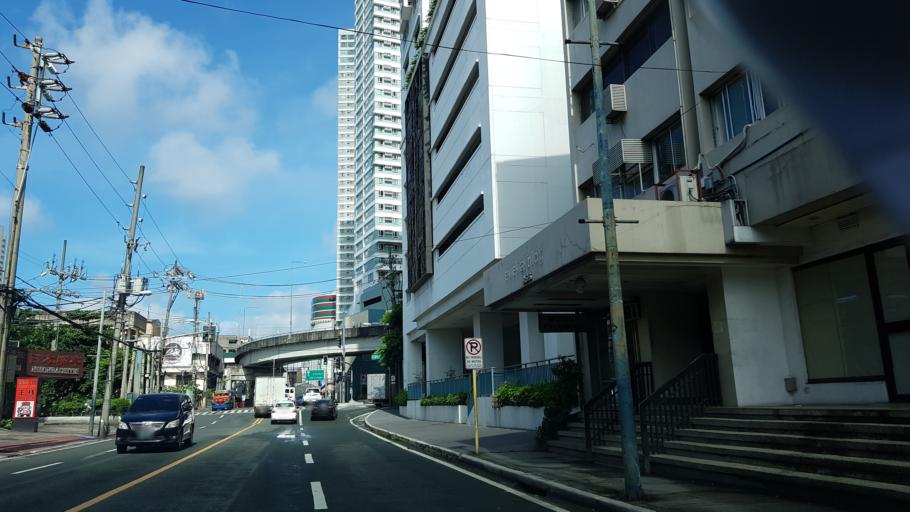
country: PH
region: Metro Manila
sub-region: Makati City
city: Makati City
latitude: 14.5511
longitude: 121.0162
